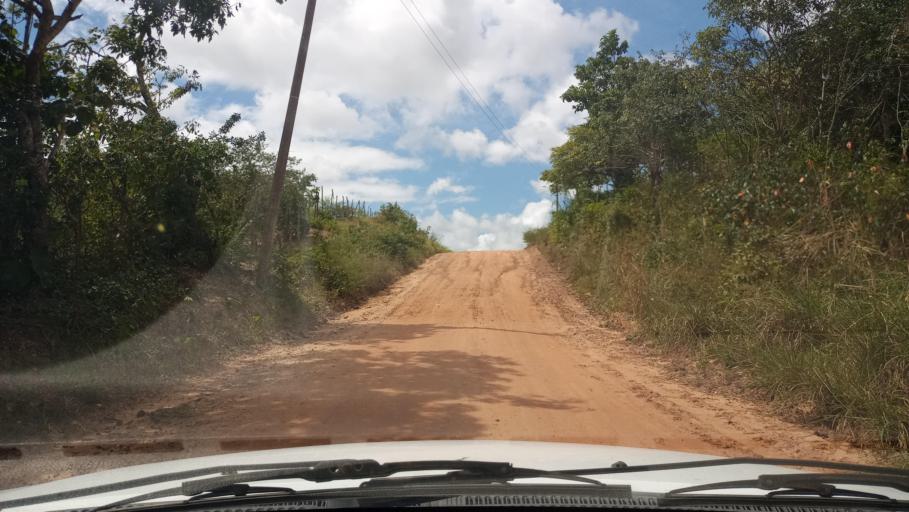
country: BR
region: Rio Grande do Norte
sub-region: Goianinha
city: Goianinha
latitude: -6.2623
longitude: -35.2627
